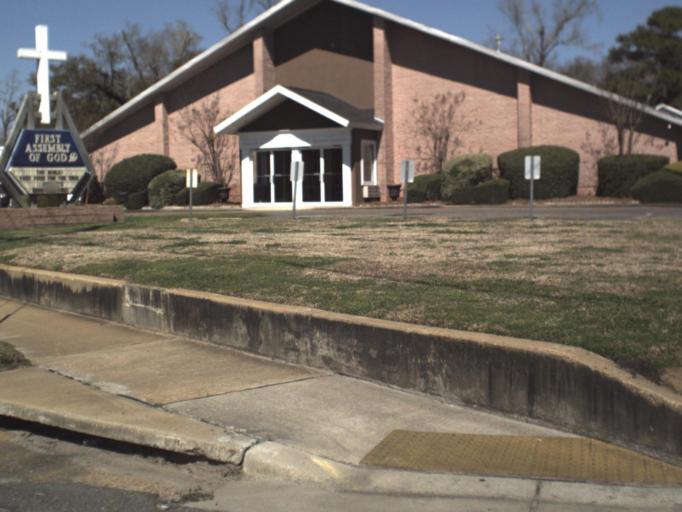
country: US
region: Florida
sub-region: Jackson County
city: Marianna
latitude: 30.7824
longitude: -85.2470
